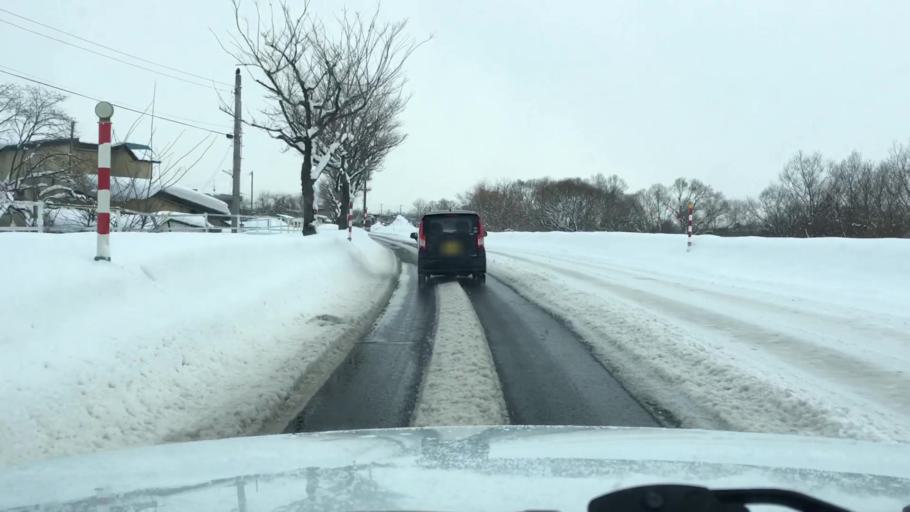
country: JP
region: Aomori
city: Hirosaki
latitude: 40.6133
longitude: 140.4559
